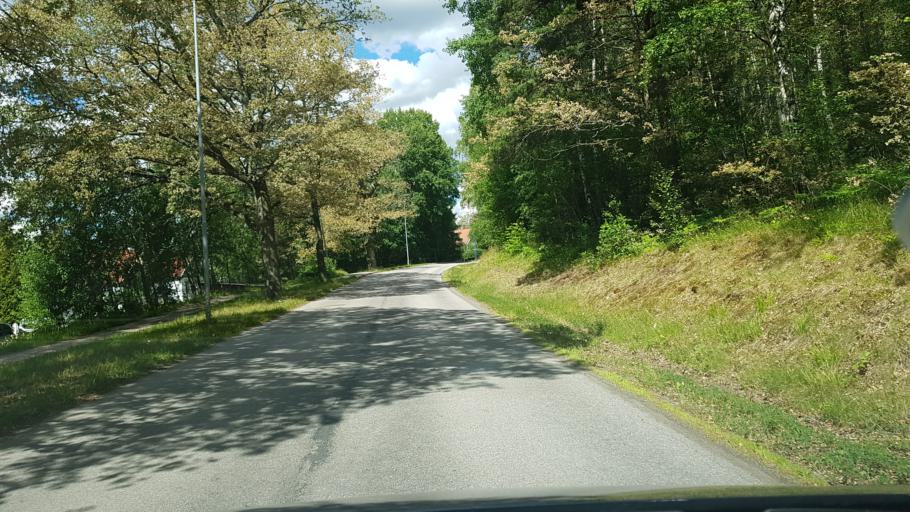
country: SE
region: Stockholm
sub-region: Upplands-Bro Kommun
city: Kungsaengen
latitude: 59.4761
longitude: 17.8065
